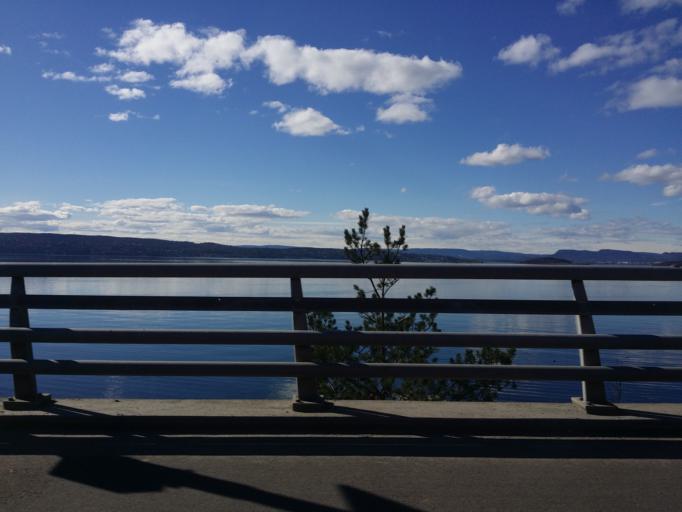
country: NO
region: Akershus
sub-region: Oppegard
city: Kolbotn
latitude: 59.8465
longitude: 10.7768
